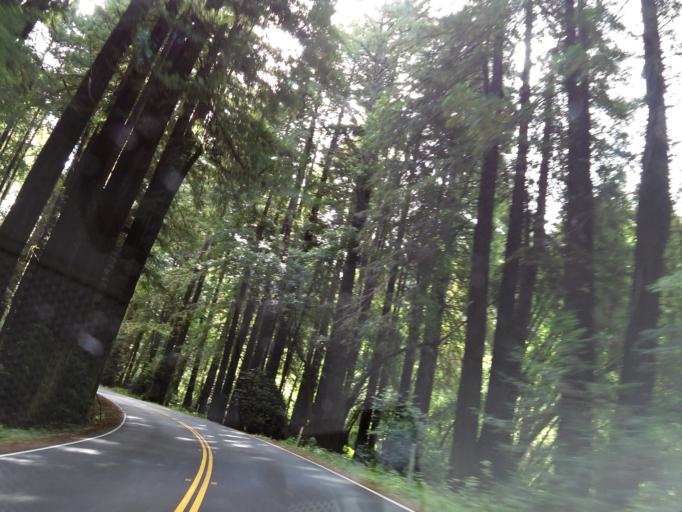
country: US
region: California
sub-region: Mendocino County
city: Boonville
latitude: 39.1571
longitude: -123.6372
